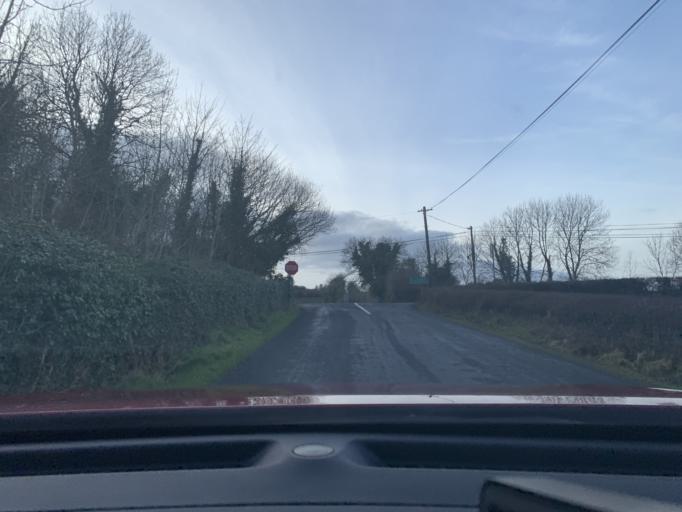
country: IE
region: Connaught
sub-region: Sligo
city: Ballymote
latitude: 54.1244
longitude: -8.5899
